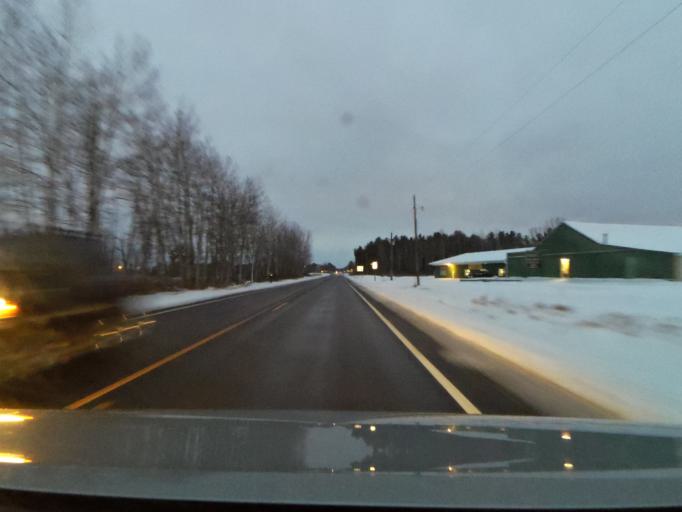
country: US
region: Wisconsin
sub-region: Dunn County
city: Menomonie
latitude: 44.9266
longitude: -91.9811
